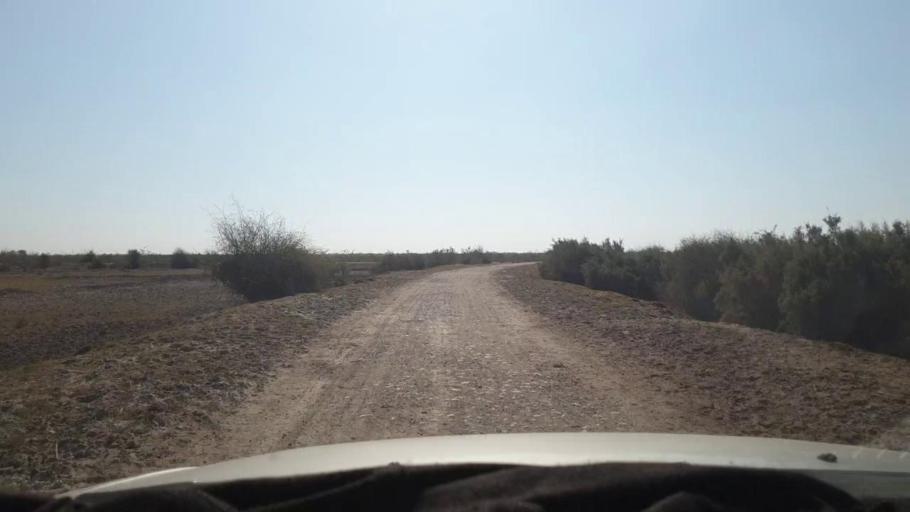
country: PK
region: Sindh
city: Adilpur
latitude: 27.8955
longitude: 69.2440
